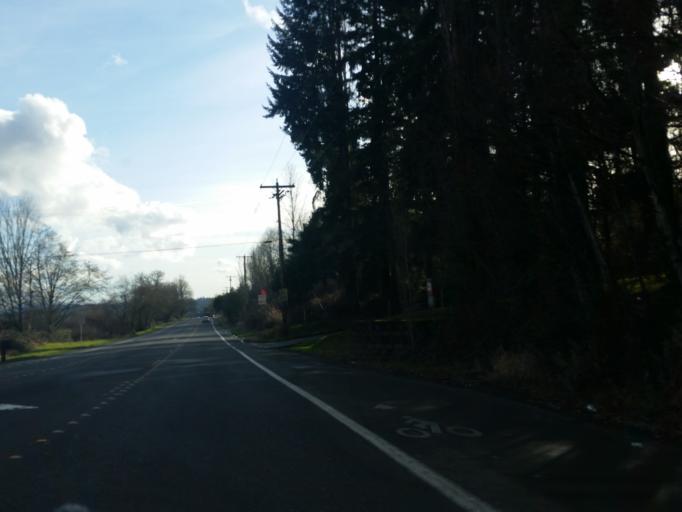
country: US
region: Washington
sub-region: King County
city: Kingsgate
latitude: 47.7100
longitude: -122.1545
